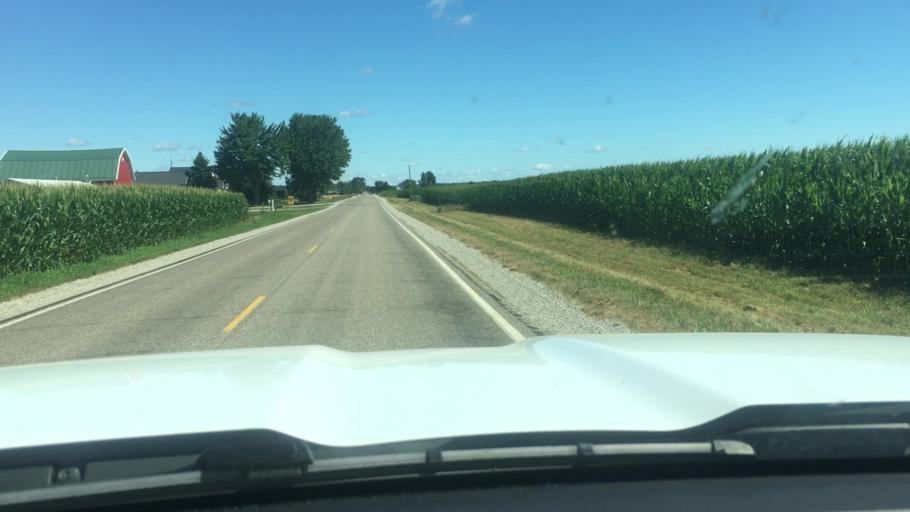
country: US
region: Michigan
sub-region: Montcalm County
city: Carson City
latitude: 43.2097
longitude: -84.7778
